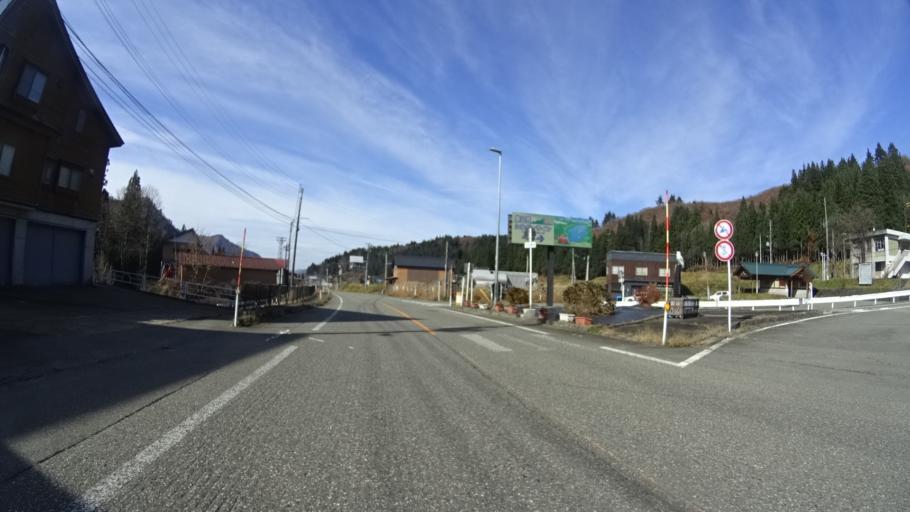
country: JP
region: Niigata
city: Muikamachi
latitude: 37.2043
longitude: 139.0722
